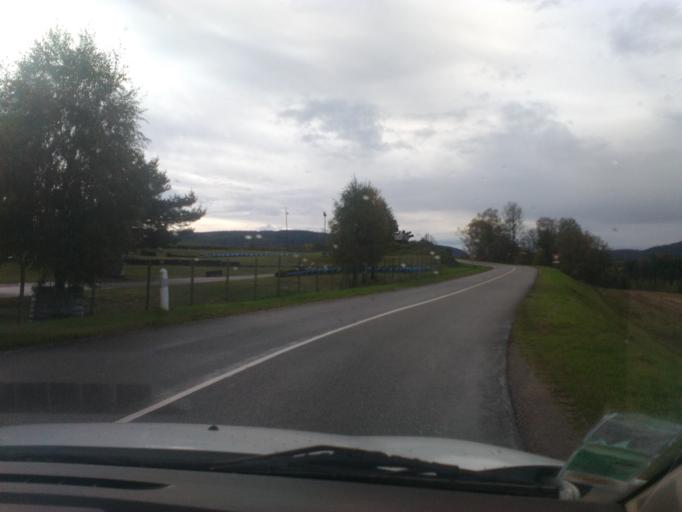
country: FR
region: Lorraine
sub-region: Departement des Vosges
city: Anould
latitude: 48.1648
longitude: 6.9171
